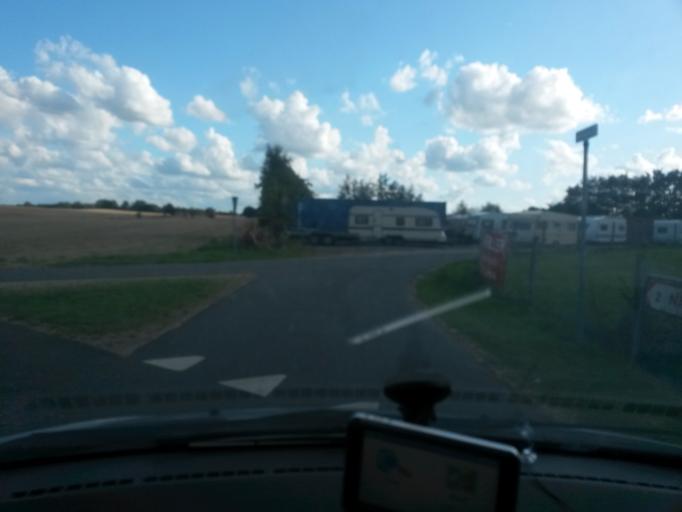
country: DK
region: Central Jutland
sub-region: Silkeborg Kommune
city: Kjellerup
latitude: 56.3261
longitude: 9.3736
